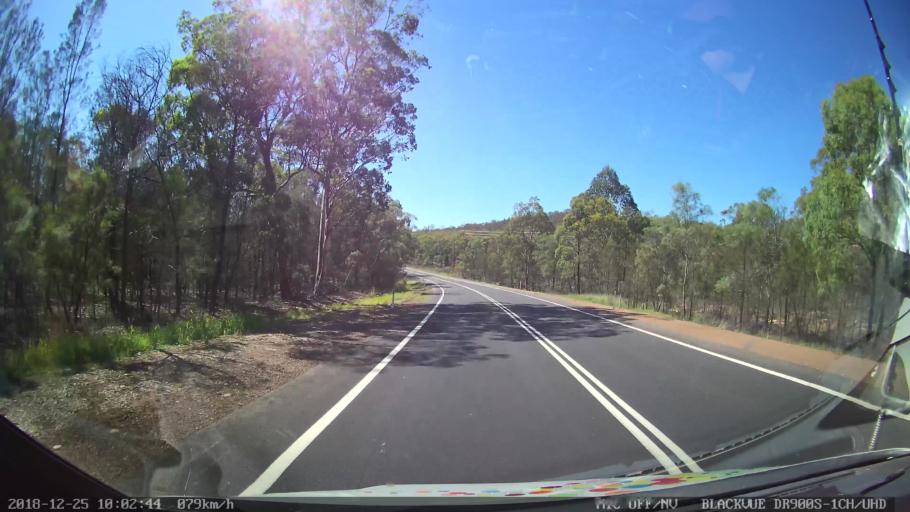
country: AU
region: New South Wales
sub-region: Upper Hunter Shire
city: Merriwa
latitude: -32.2216
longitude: 150.4650
